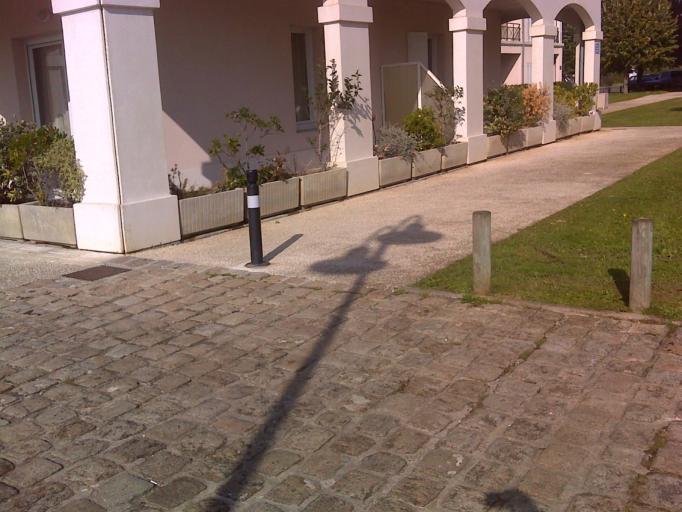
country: FR
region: Poitou-Charentes
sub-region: Departement de la Charente-Maritime
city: Rochefort
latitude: 45.9460
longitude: -0.9596
